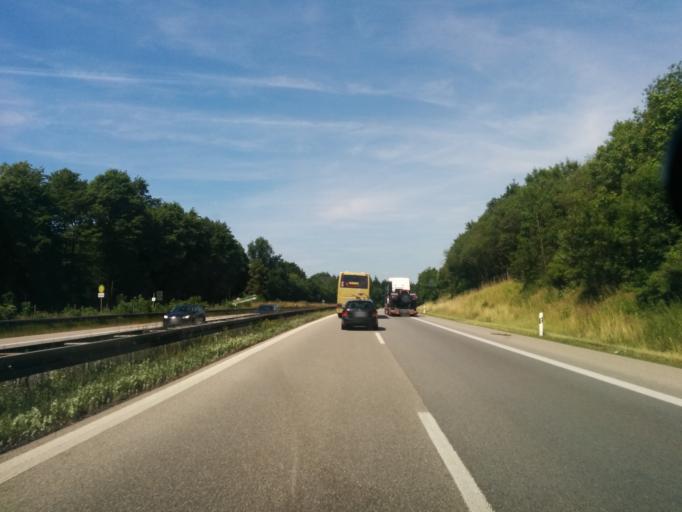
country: DE
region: Bavaria
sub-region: Upper Bavaria
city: Wessling
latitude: 48.0921
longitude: 11.2571
